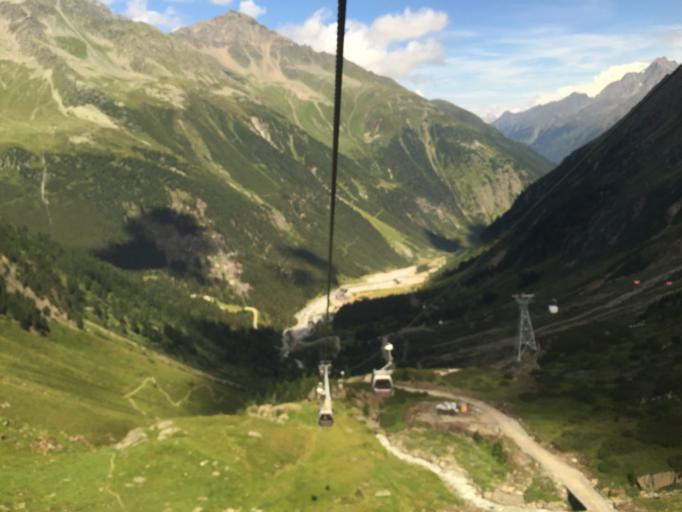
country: AT
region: Tyrol
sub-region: Politischer Bezirk Imst
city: Soelden
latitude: 47.0006
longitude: 11.1443
